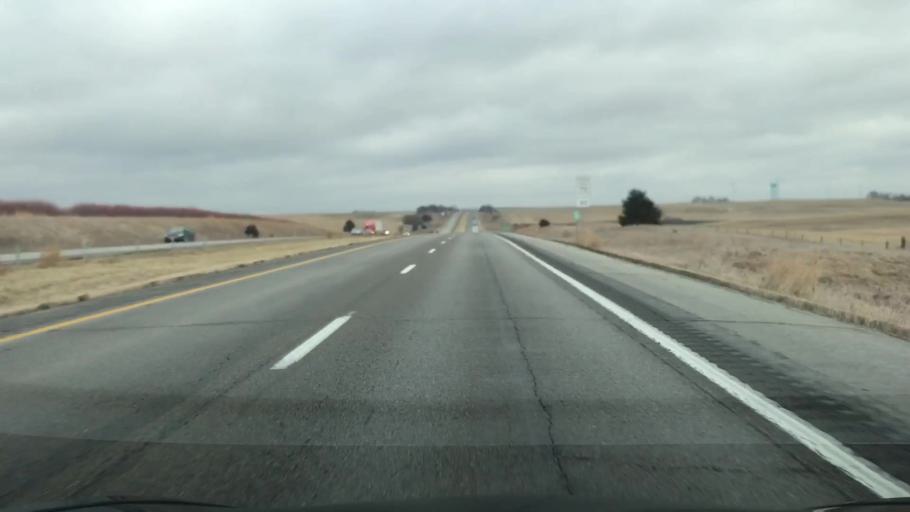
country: US
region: Iowa
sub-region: Guthrie County
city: Stuart
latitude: 41.4958
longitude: -94.4005
